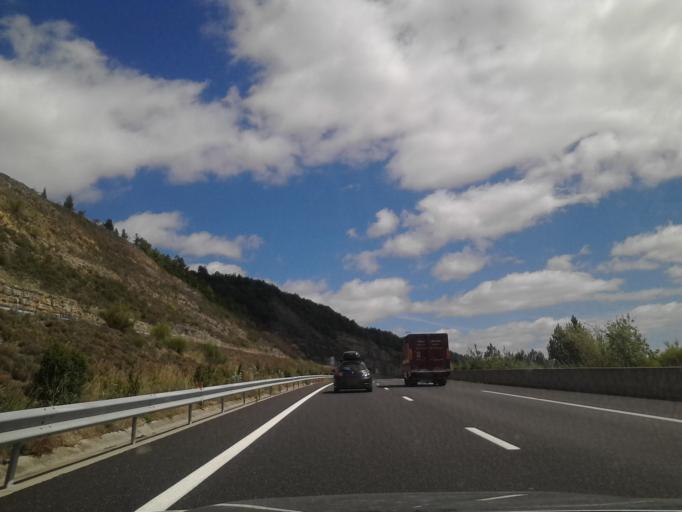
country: FR
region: Languedoc-Roussillon
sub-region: Departement de la Lozere
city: Chirac
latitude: 44.4908
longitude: 3.2218
